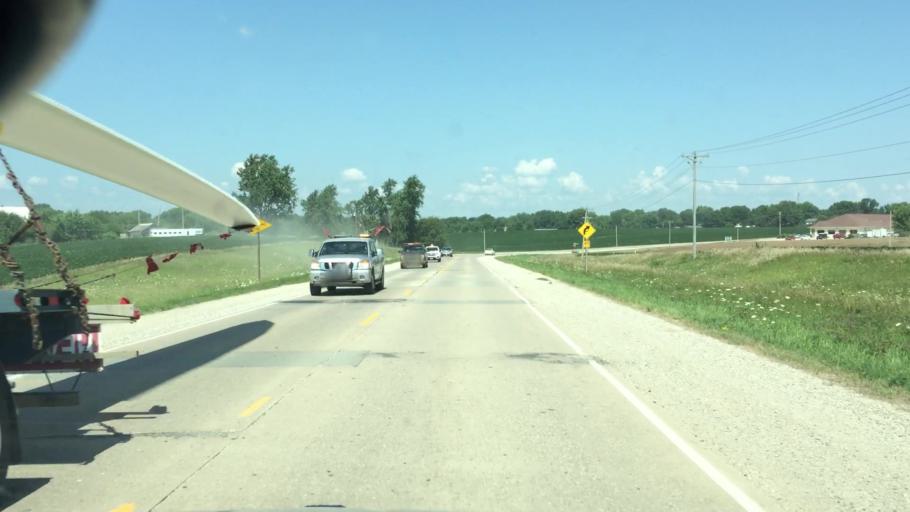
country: US
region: Iowa
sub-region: Jasper County
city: Newton
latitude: 41.6902
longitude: -93.0121
